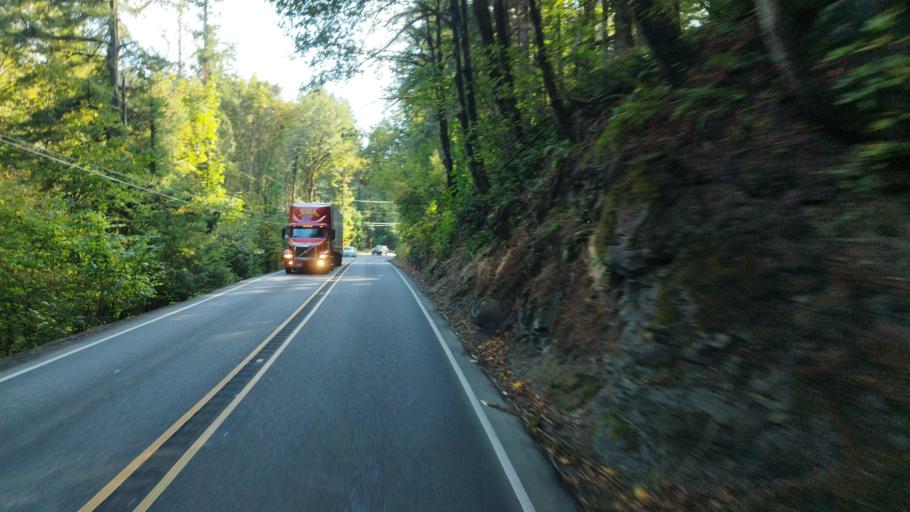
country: US
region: Oregon
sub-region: Washington County
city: Bethany
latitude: 45.6349
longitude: -122.8634
